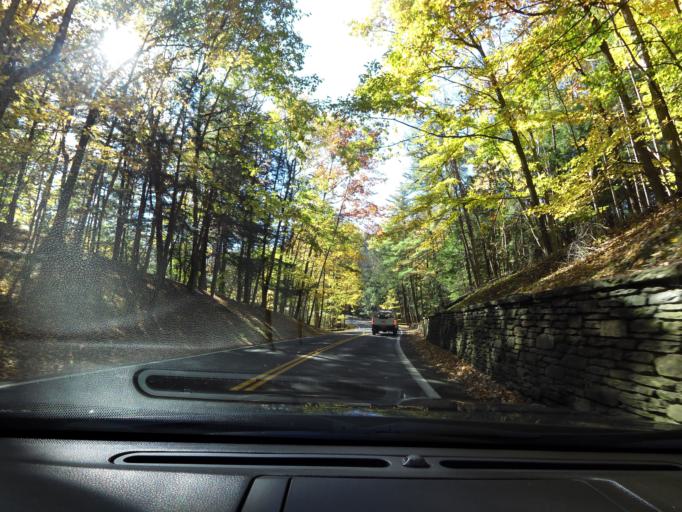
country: US
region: New York
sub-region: Wyoming County
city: Castile
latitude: 42.5801
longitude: -78.0498
